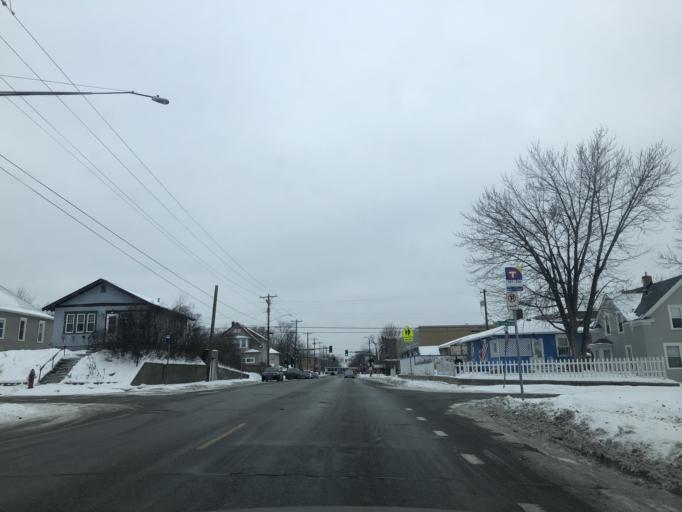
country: US
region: Minnesota
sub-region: Anoka County
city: Columbia Heights
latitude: 45.0240
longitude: -93.2928
